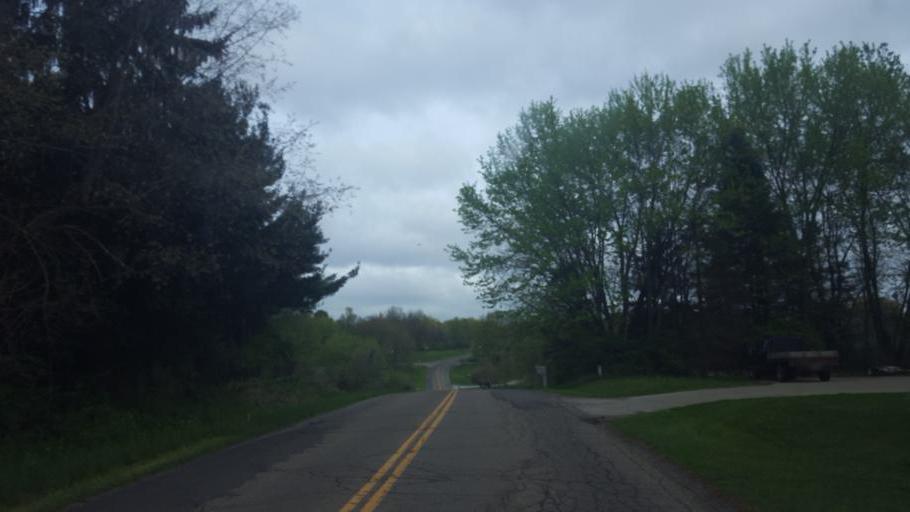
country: US
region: Ohio
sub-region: Knox County
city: Gambier
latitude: 40.4310
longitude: -82.3622
